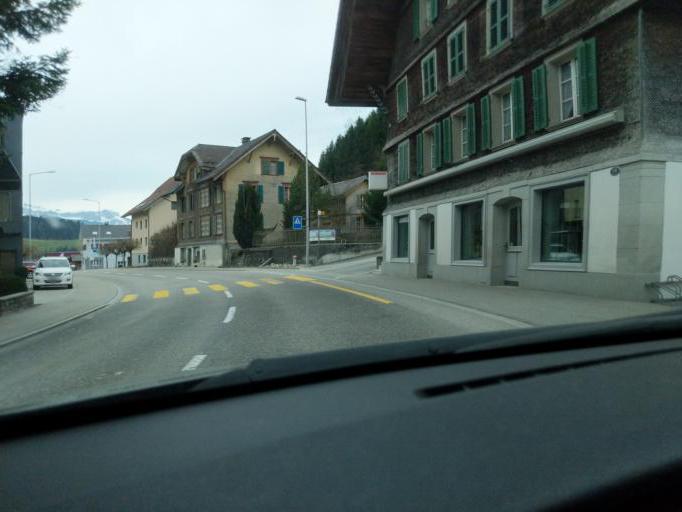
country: CH
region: Lucerne
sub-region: Entlebuch District
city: Escholzmatt
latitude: 46.9134
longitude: 7.9335
